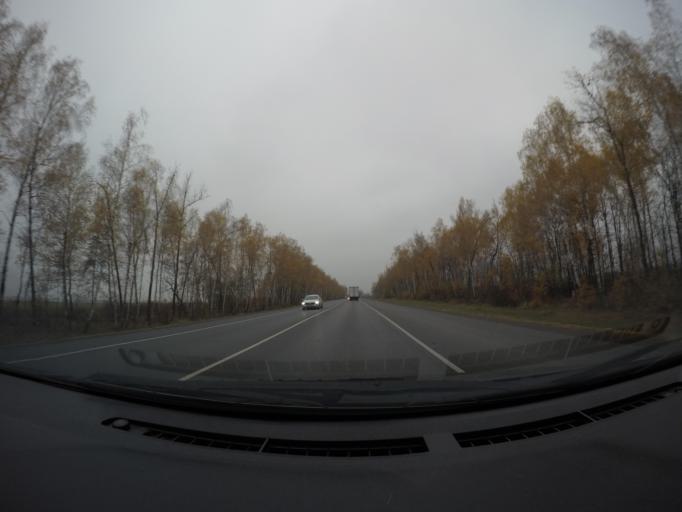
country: RU
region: Moskovskaya
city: Zhitnevo
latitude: 55.3629
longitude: 38.0070
